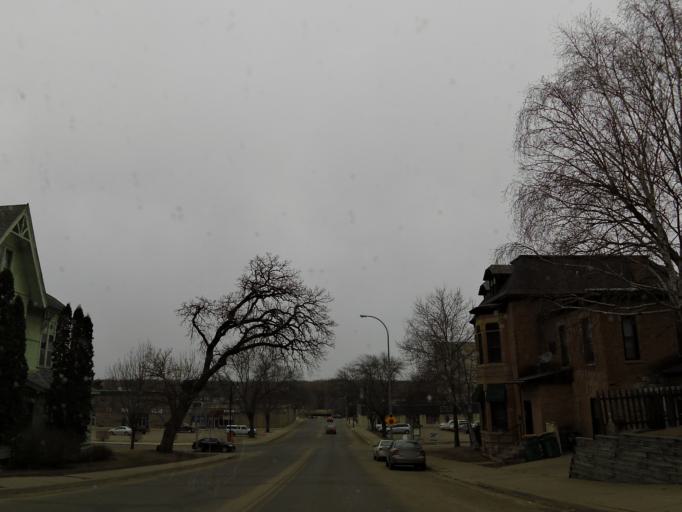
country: US
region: Minnesota
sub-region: Le Sueur County
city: Le Sueur
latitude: 44.4606
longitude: -93.9136
